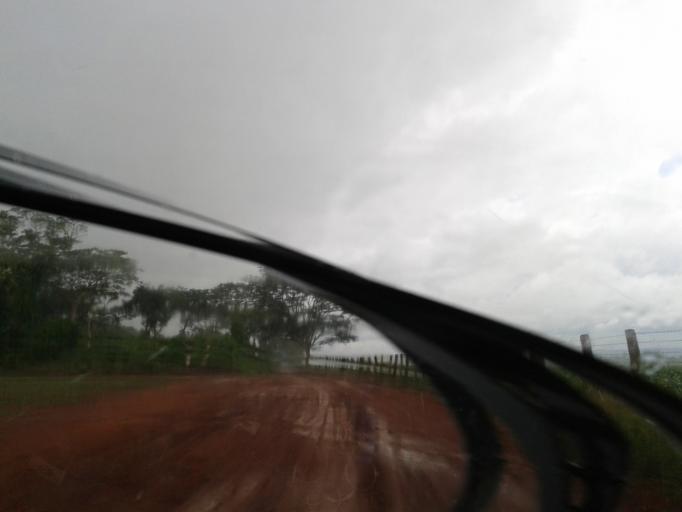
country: BR
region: Minas Gerais
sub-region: Santa Vitoria
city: Santa Vitoria
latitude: -18.6504
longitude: -49.9129
